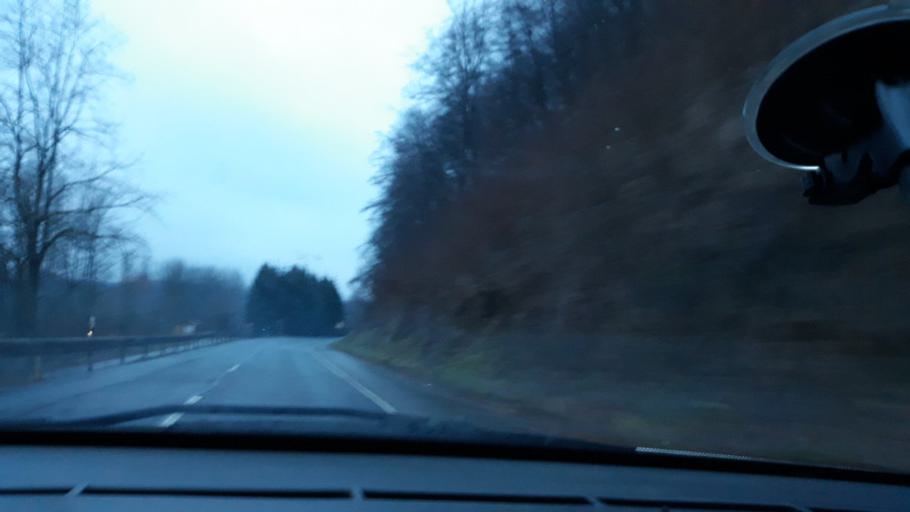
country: DE
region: Saarland
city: Blieskastel
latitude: 49.2212
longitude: 7.2579
